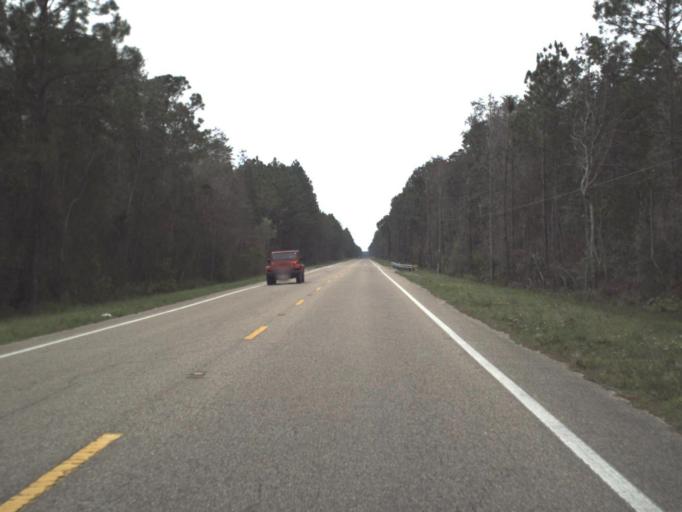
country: US
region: Florida
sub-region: Gulf County
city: Port Saint Joe
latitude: 29.8633
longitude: -85.2416
